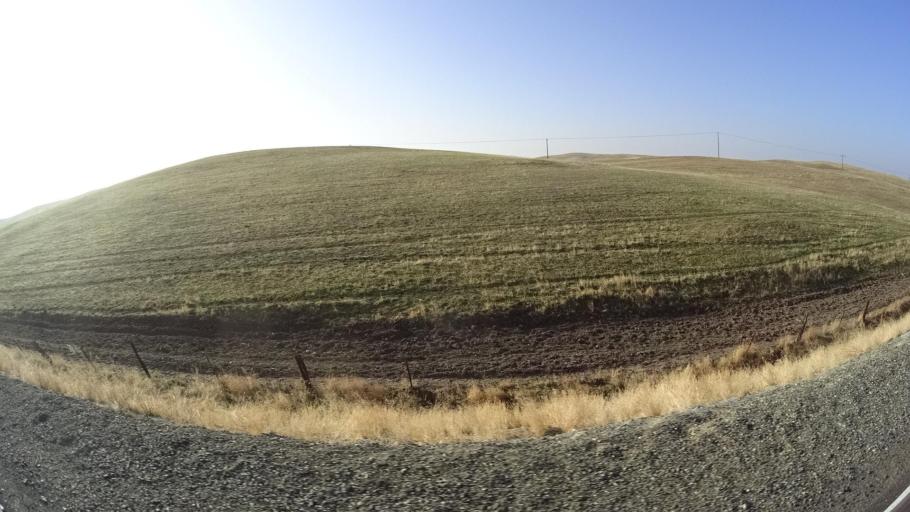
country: US
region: California
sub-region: Tulare County
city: Richgrove
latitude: 35.7494
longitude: -118.9920
